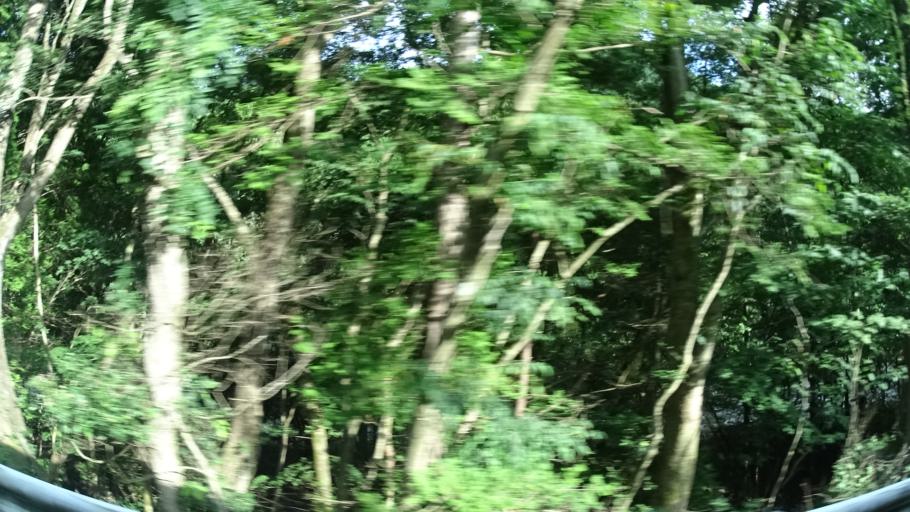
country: JP
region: Tochigi
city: Nikko
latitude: 36.6691
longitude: 139.4771
